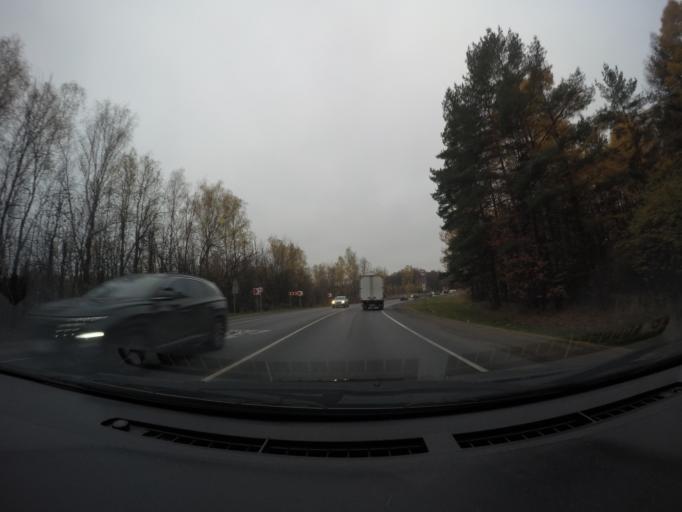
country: RU
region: Moskovskaya
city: Bronnitsy
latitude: 55.3997
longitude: 38.2262
